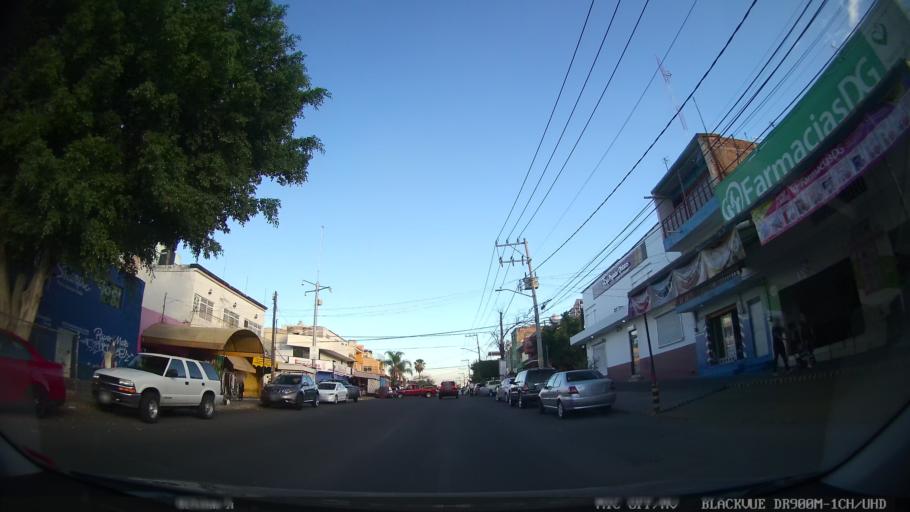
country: MX
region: Jalisco
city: Tlaquepaque
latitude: 20.7033
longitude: -103.2924
